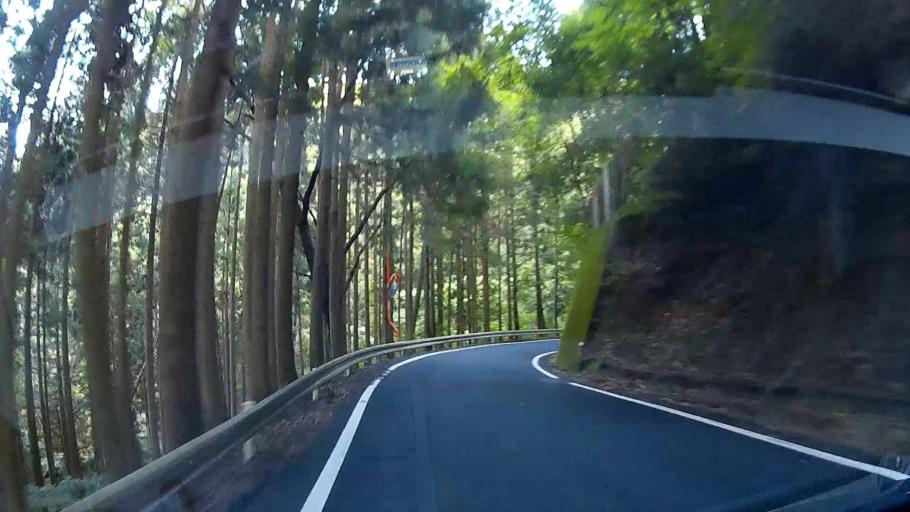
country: JP
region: Shizuoka
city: Shizuoka-shi
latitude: 35.1362
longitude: 138.2708
